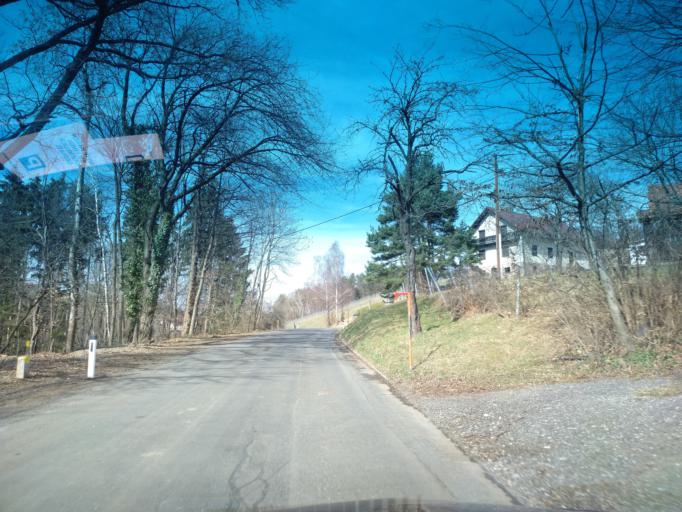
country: AT
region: Styria
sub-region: Politischer Bezirk Leibnitz
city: Sankt Nikolai im Sausal
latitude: 46.7986
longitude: 15.4312
